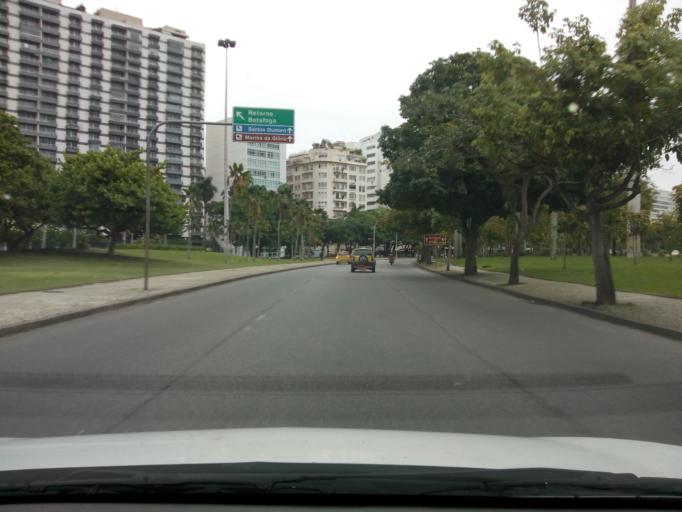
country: BR
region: Rio de Janeiro
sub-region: Rio De Janeiro
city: Rio de Janeiro
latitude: -22.9378
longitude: -43.1724
